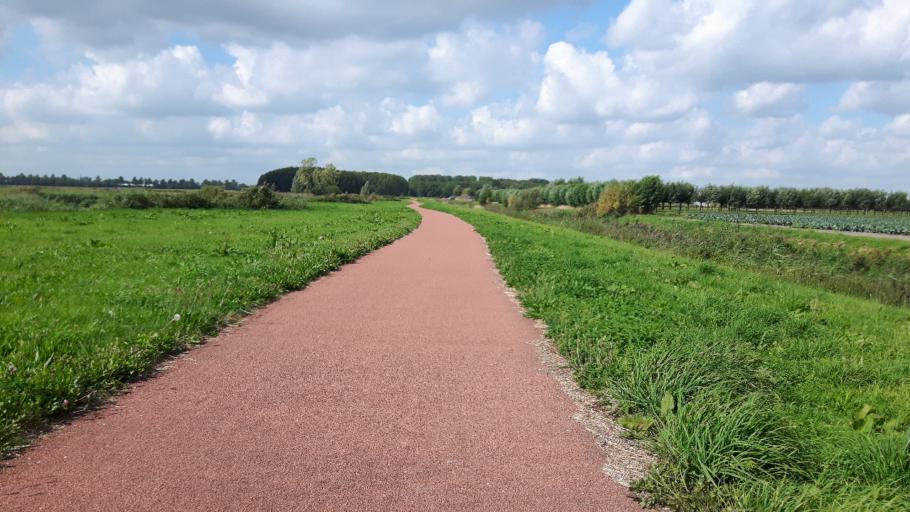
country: NL
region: North Holland
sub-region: Gemeente Enkhuizen
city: Enkhuizen
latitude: 52.7169
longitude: 5.2453
